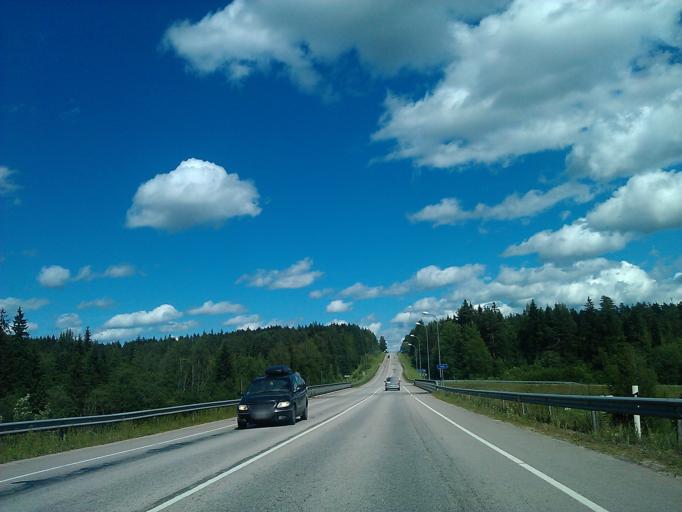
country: LV
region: Amatas Novads
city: Drabesi
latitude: 57.2218
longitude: 25.2333
